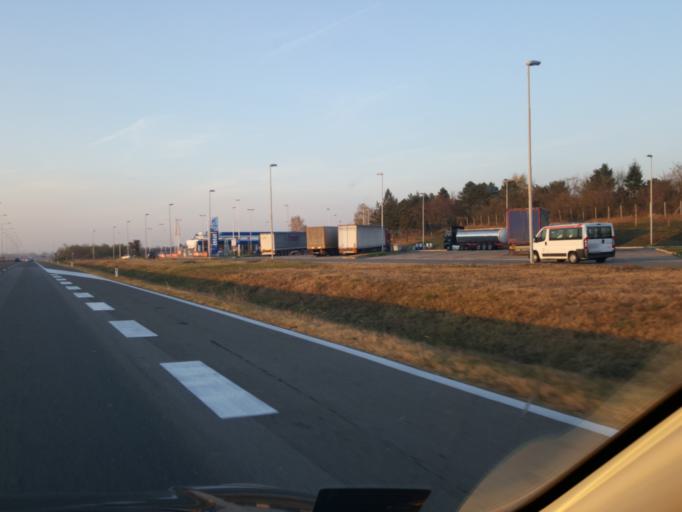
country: RS
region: Central Serbia
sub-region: Nisavski Okrug
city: Nis
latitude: 43.3836
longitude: 21.8075
